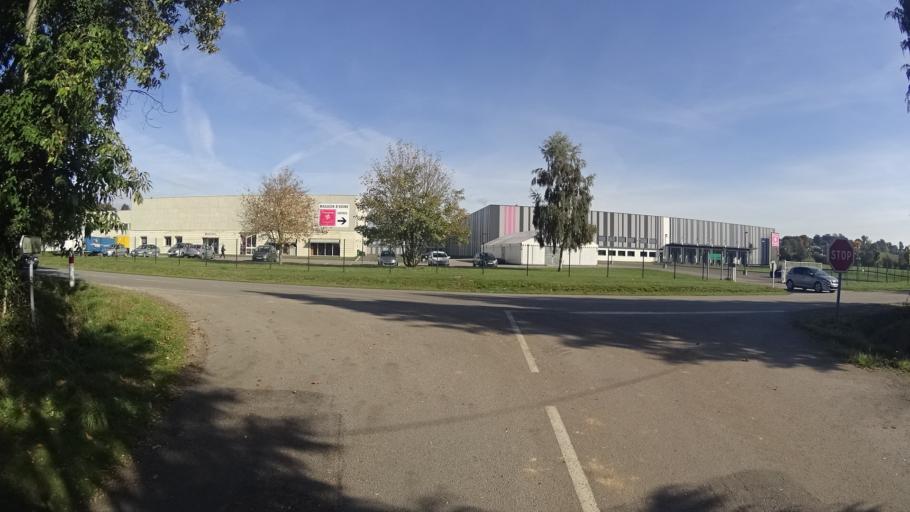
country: FR
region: Brittany
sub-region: Departement du Morbihan
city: Peillac
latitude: 47.7366
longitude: -2.2201
